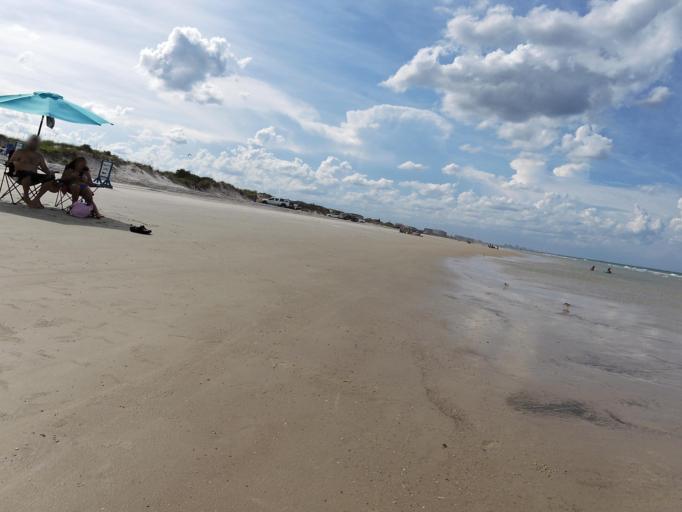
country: US
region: Florida
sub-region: Volusia County
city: Ponce Inlet
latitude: 29.0812
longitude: -80.9211
